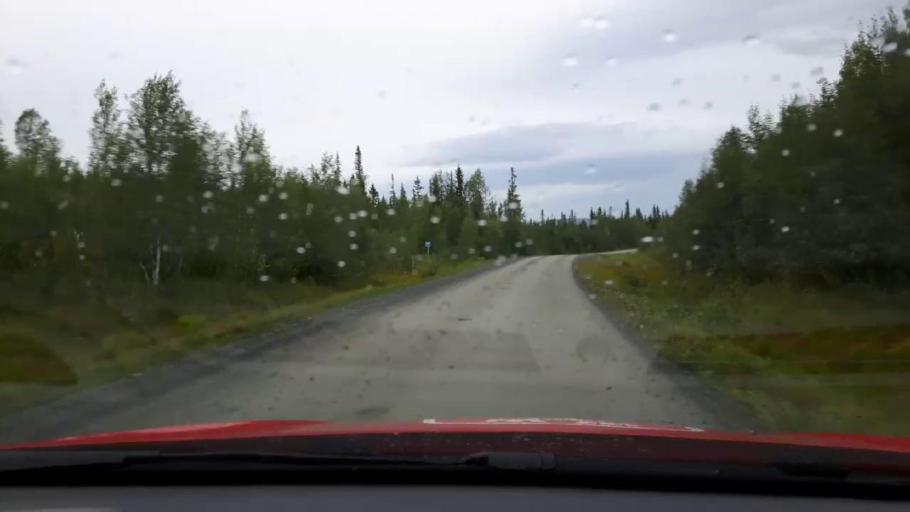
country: SE
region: Jaemtland
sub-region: Are Kommun
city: Are
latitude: 63.4225
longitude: 13.2176
